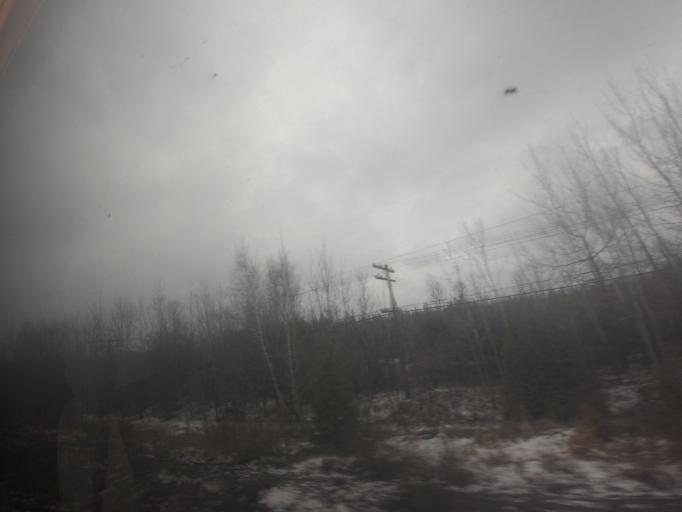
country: CA
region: Ontario
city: Cobourg
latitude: 43.9538
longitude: -78.2398
